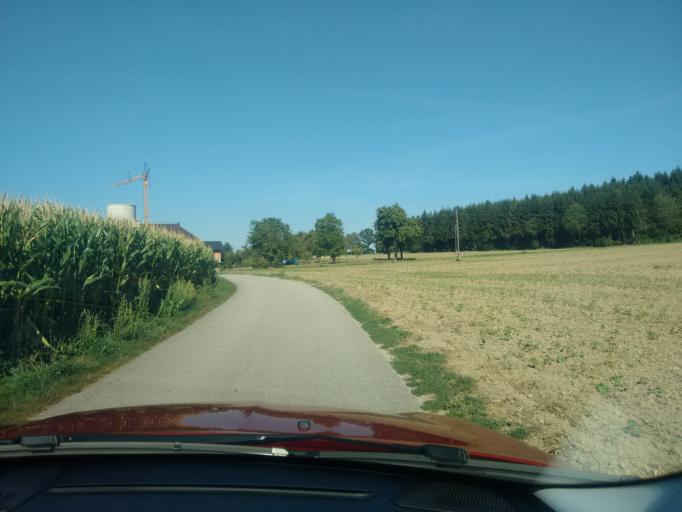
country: AT
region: Upper Austria
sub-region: Wels-Land
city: Sattledt
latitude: 48.0918
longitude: 14.0667
